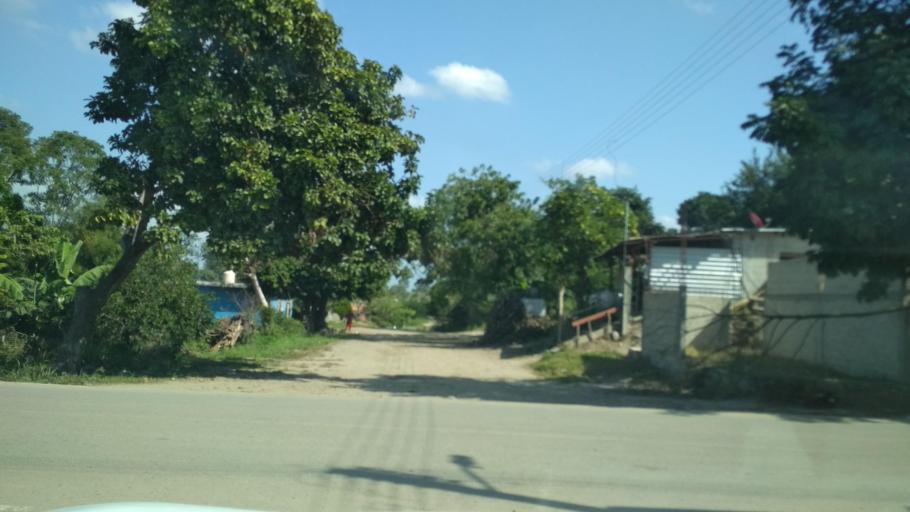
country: MX
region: Puebla
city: San Jose Acateno
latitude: 20.1903
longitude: -97.1563
